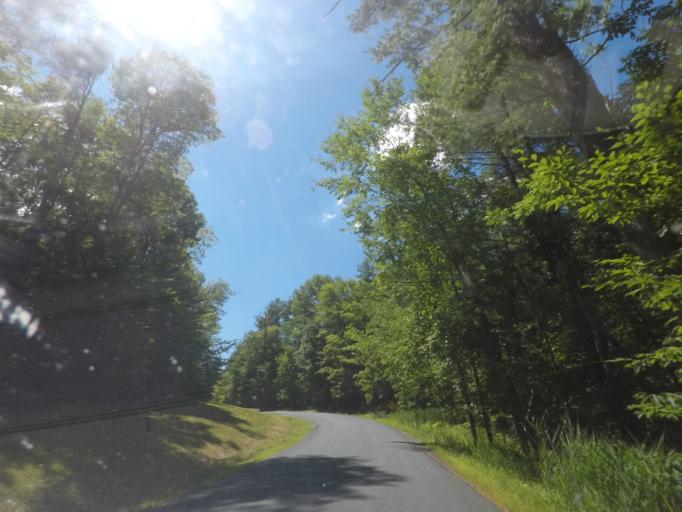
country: US
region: New York
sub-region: Rensselaer County
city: Averill Park
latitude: 42.5759
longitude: -73.5203
